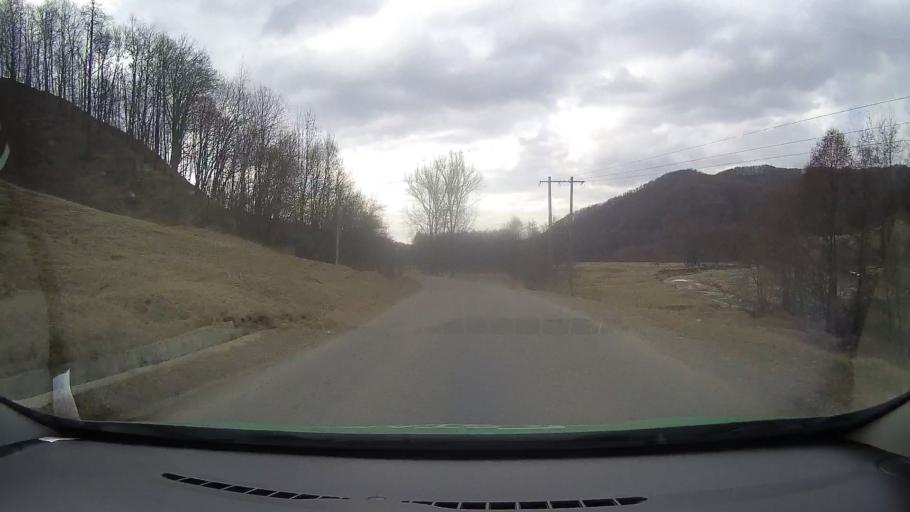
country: RO
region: Dambovita
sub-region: Comuna Visinesti
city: Visinesti
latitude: 45.0953
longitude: 25.5783
